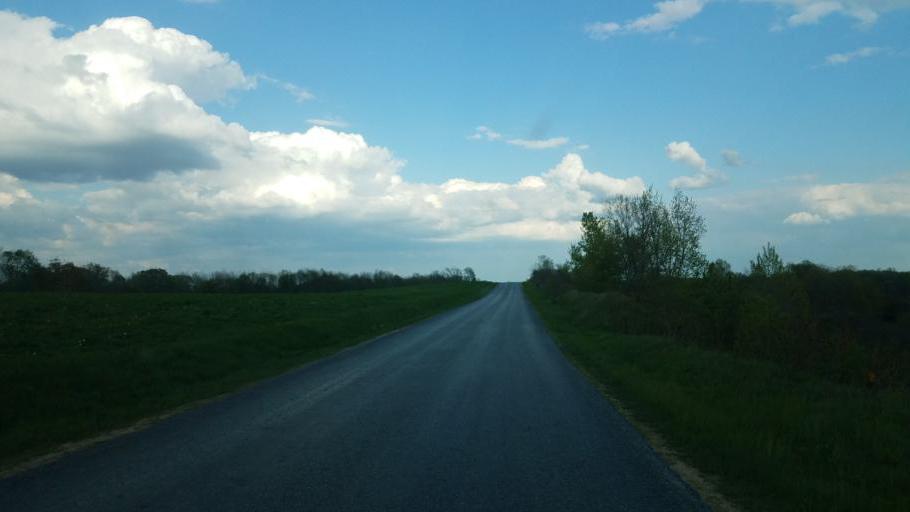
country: US
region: Wisconsin
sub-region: Vernon County
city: Hillsboro
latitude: 43.6849
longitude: -90.3815
